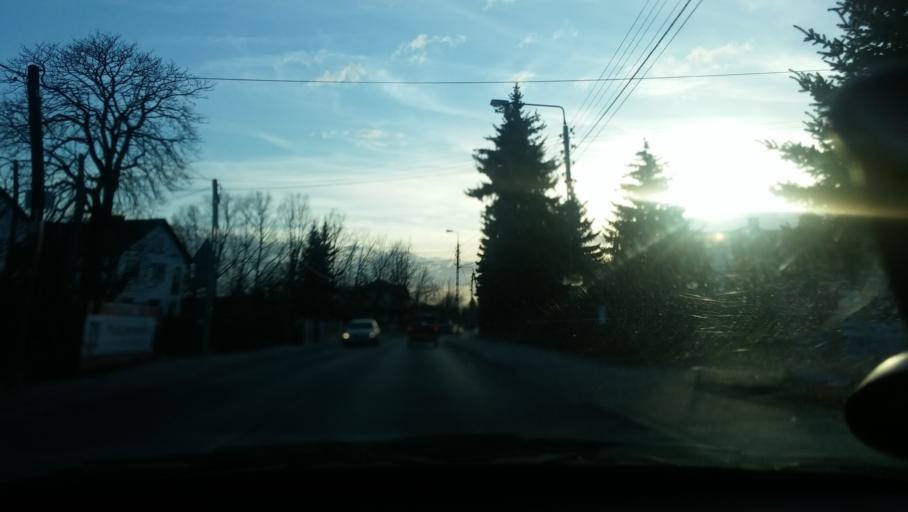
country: PL
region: Masovian Voivodeship
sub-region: Warszawa
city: Wawer
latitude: 52.1991
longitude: 21.1439
